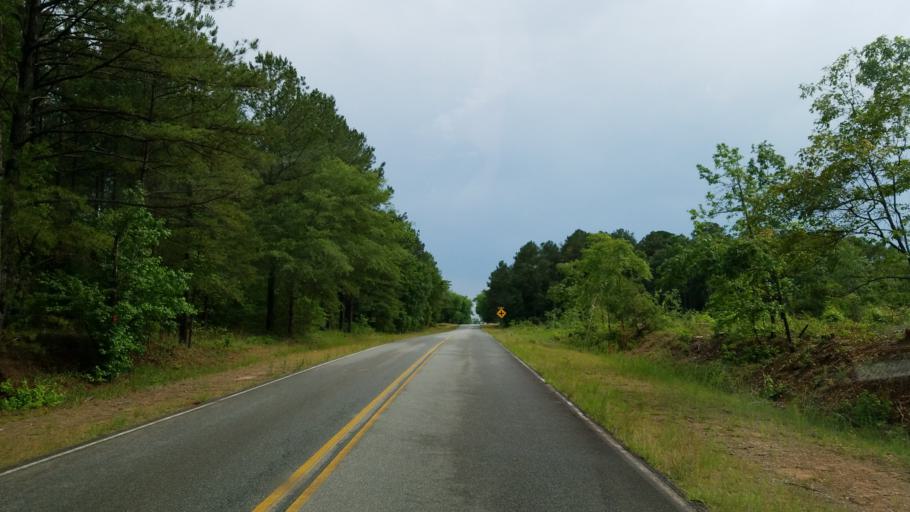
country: US
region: Georgia
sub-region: Dooly County
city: Unadilla
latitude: 32.3115
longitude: -83.7899
